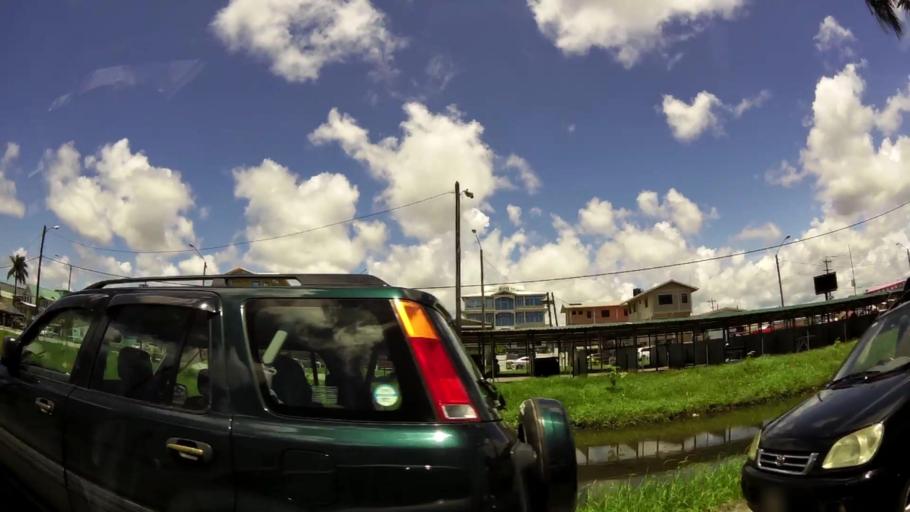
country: GY
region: Demerara-Mahaica
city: Georgetown
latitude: 6.8112
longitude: -58.1566
